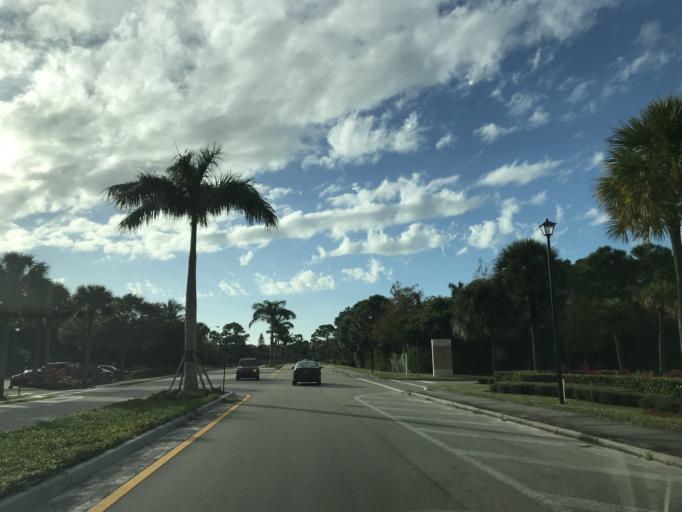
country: US
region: Florida
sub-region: Palm Beach County
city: Jupiter
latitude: 26.9213
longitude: -80.0965
